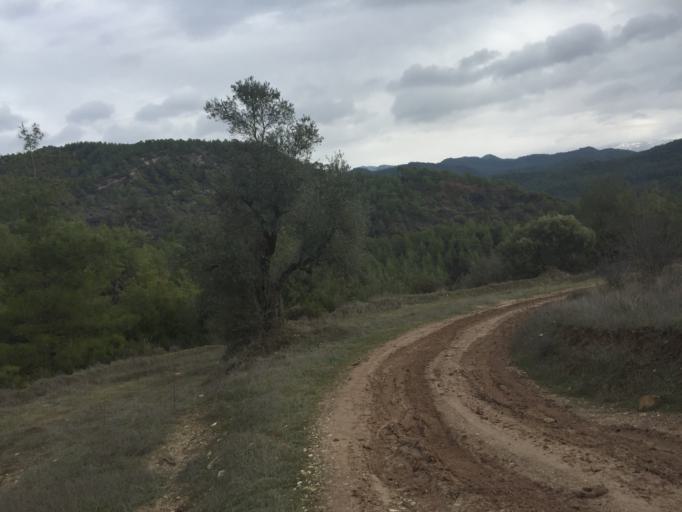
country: CY
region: Limassol
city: Pachna
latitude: 34.8869
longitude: 32.6720
